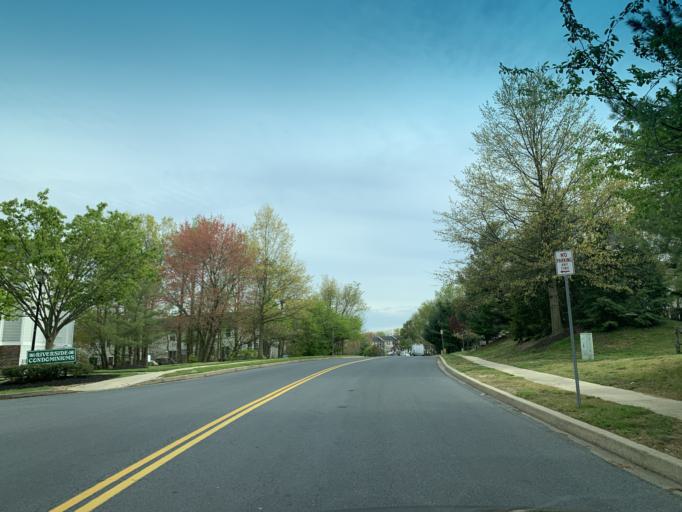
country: US
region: Maryland
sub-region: Harford County
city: Riverside
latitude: 39.4795
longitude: -76.2538
